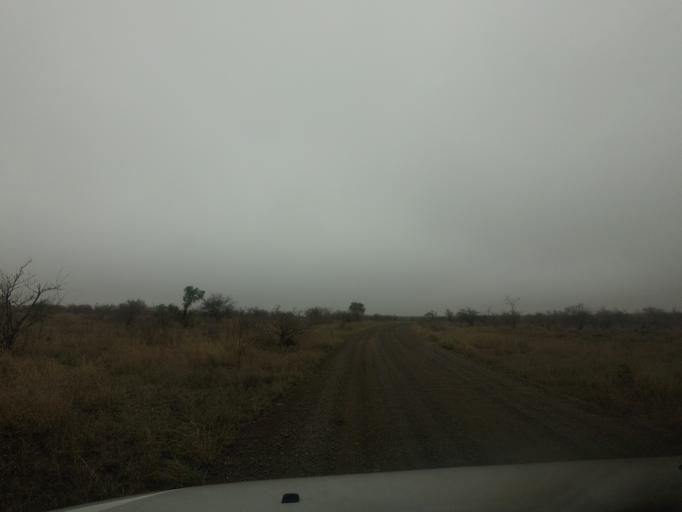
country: ZA
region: Limpopo
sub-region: Mopani District Municipality
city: Phalaborwa
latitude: -24.2622
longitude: 31.6572
